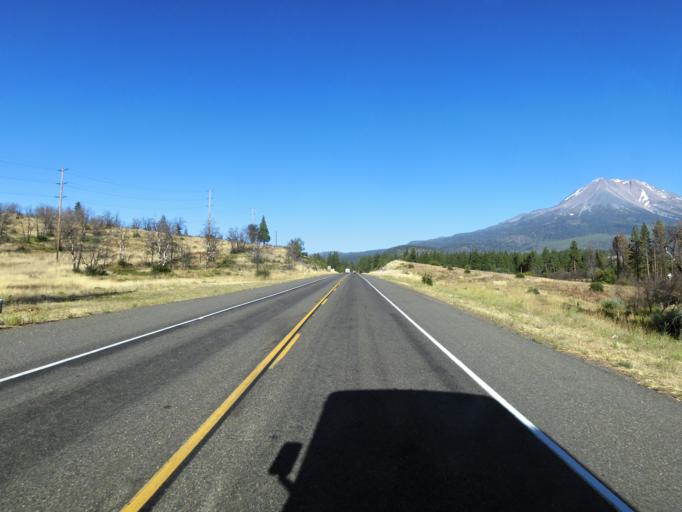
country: US
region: California
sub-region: Siskiyou County
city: Weed
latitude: 41.4411
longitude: -122.3842
